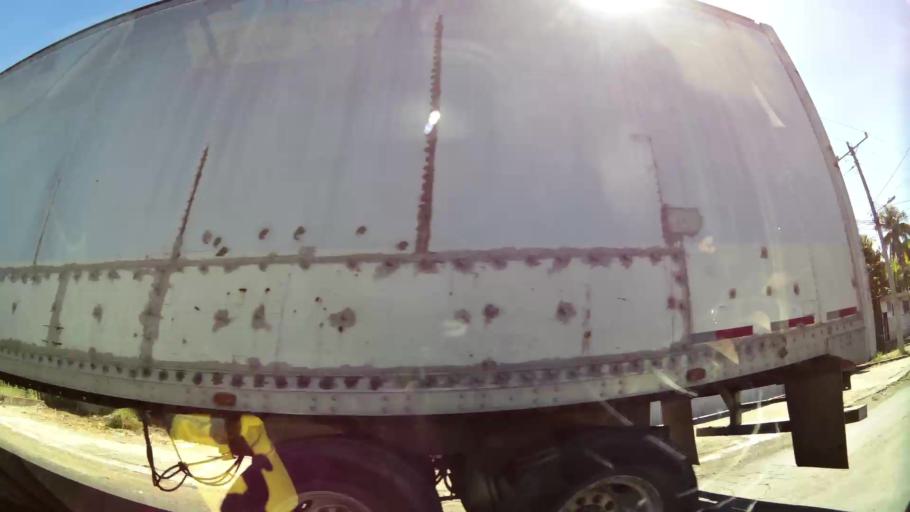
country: SV
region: La Libertad
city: San Juan Opico
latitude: 13.7874
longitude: -89.3705
